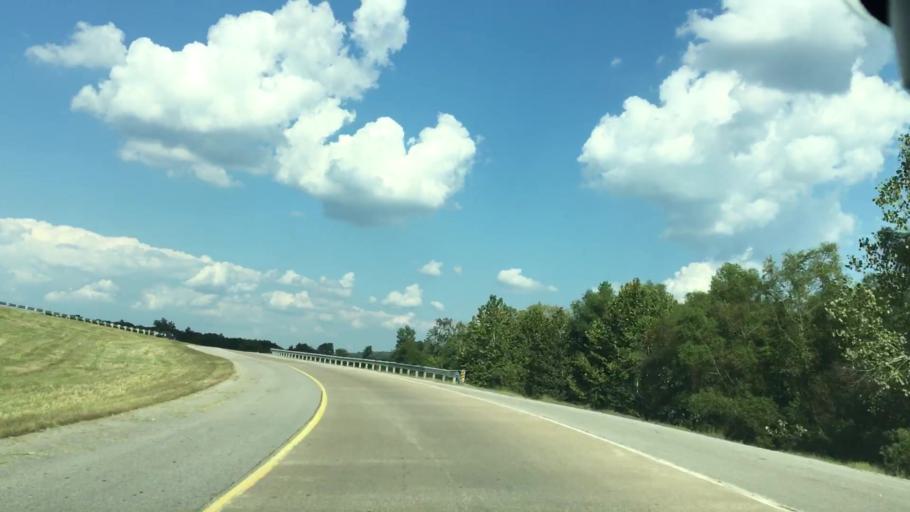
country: US
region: Tennessee
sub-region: Wilson County
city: Mount Juliet
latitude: 36.2325
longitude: -86.4279
